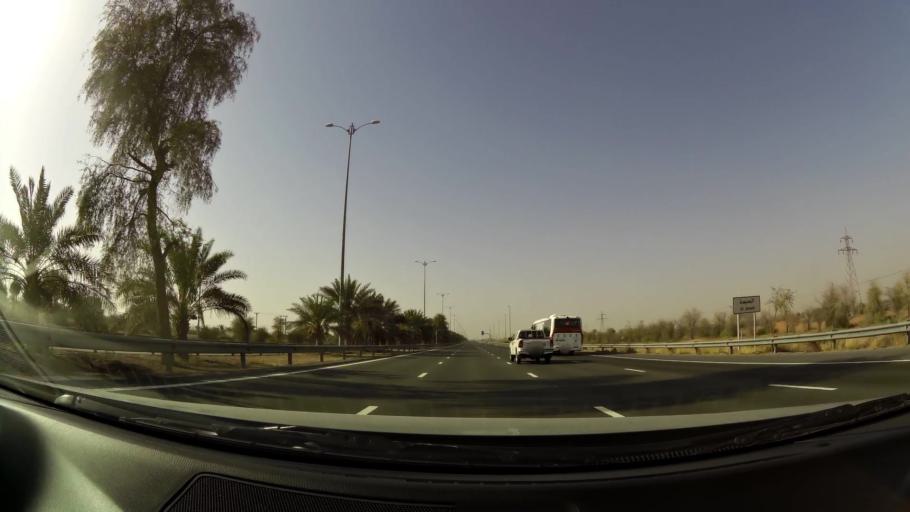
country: OM
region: Al Buraimi
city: Al Buraymi
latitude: 24.5271
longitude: 55.7606
